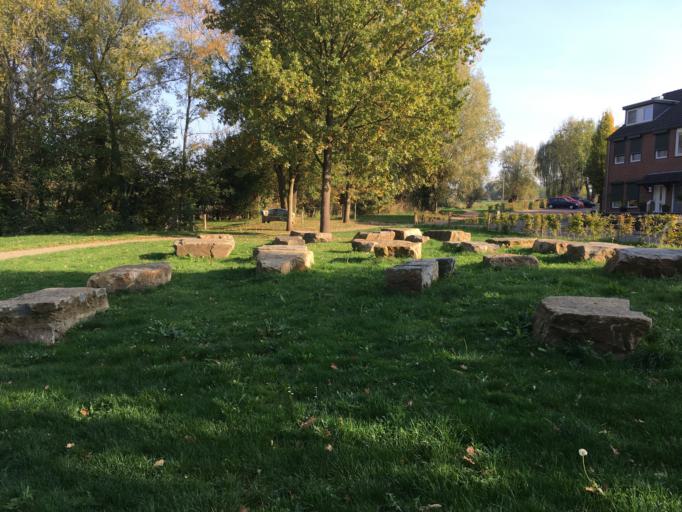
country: NL
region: Limburg
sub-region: Gemeente Voerendaal
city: Ubachsberg
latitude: 50.7956
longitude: 5.9285
